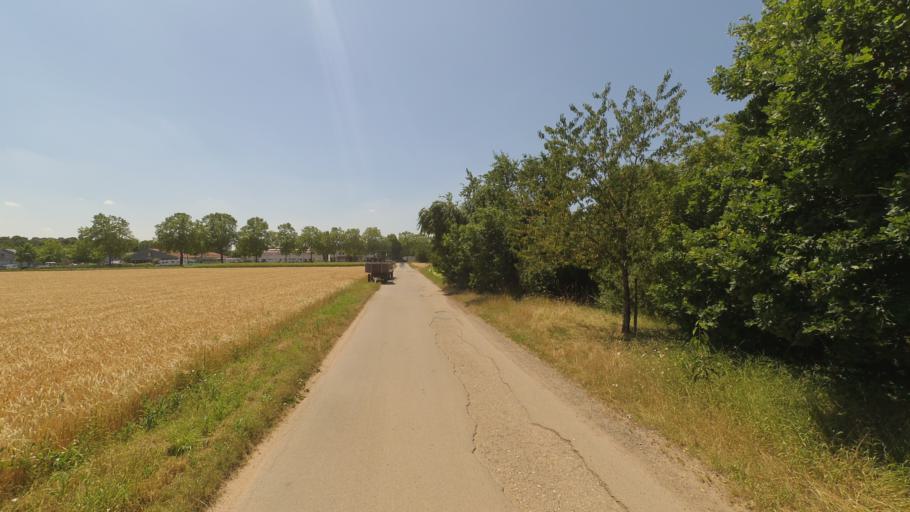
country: DE
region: Baden-Wuerttemberg
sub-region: Karlsruhe Region
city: Schwetzingen
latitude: 49.3792
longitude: 8.5590
